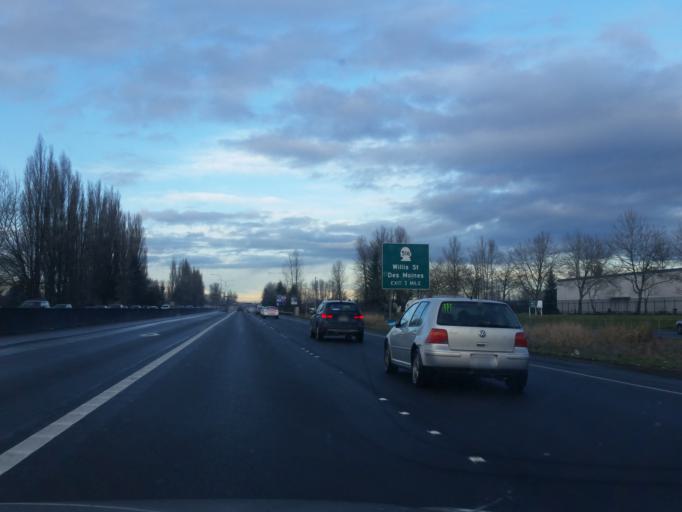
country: US
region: Washington
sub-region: King County
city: Kent
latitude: 47.3602
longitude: -122.2446
